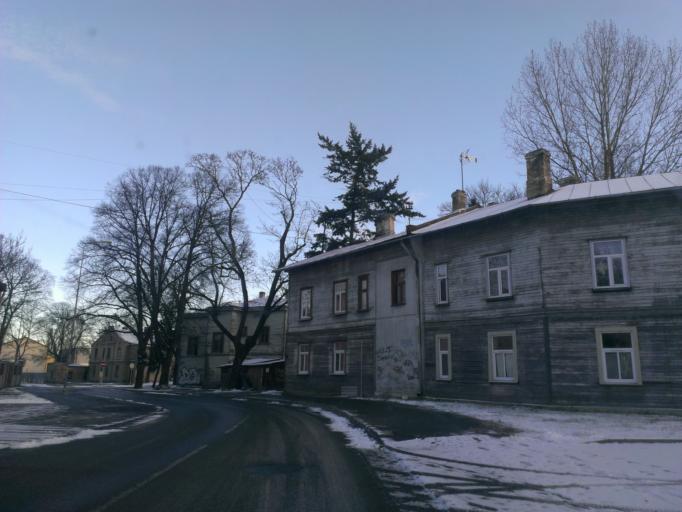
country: LV
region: Riga
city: Riga
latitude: 56.9528
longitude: 24.0691
